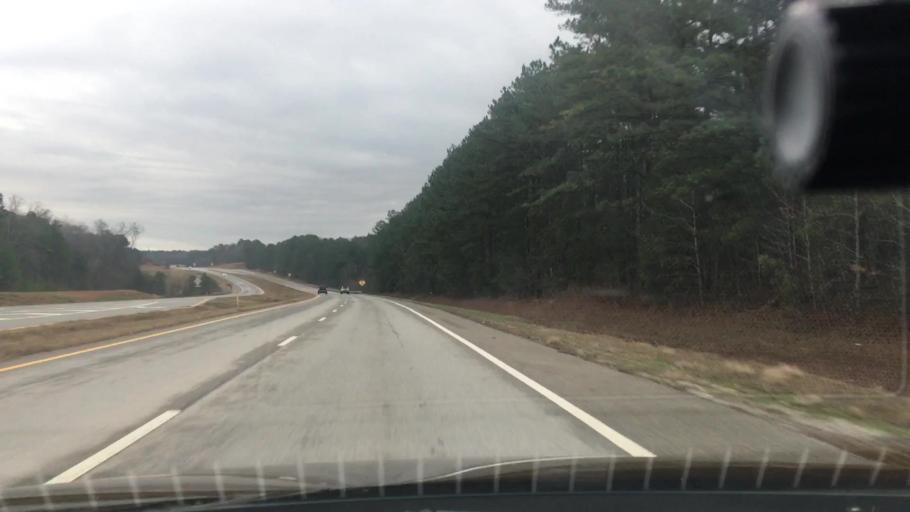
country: US
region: Georgia
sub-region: Henry County
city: Locust Grove
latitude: 33.2586
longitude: -84.1137
